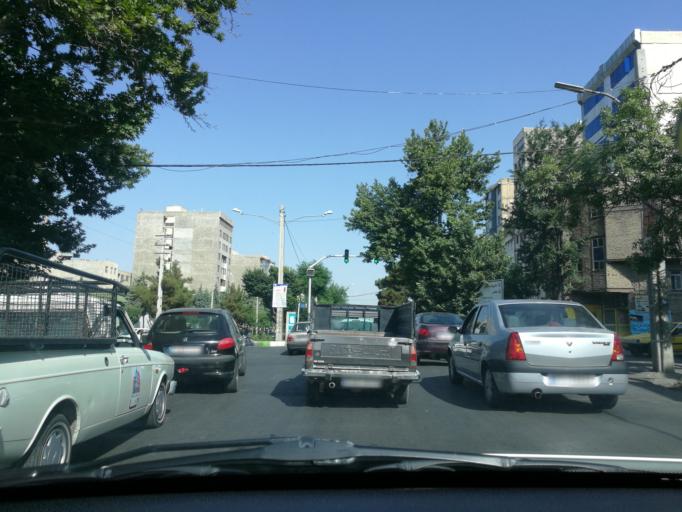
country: IR
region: Alborz
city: Karaj
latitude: 35.8562
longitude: 50.9538
